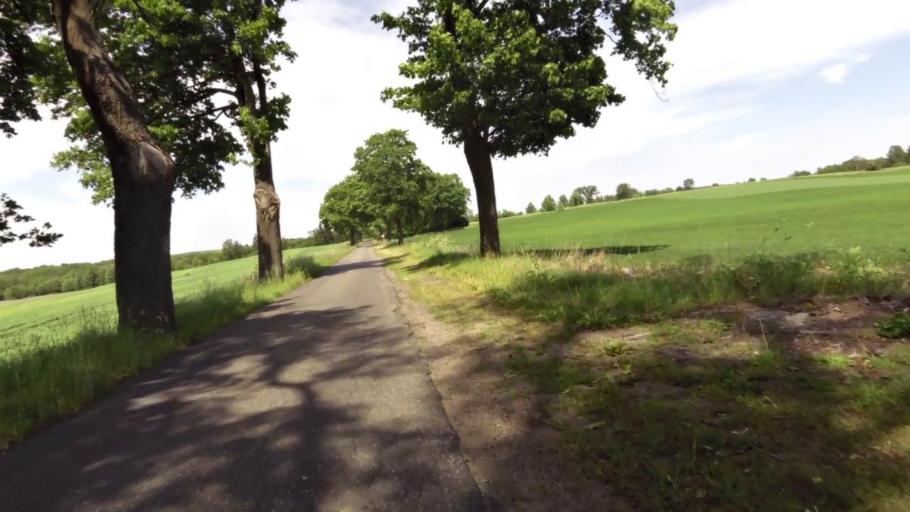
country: PL
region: West Pomeranian Voivodeship
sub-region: Powiat szczecinecki
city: Szczecinek
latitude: 53.6384
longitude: 16.6839
